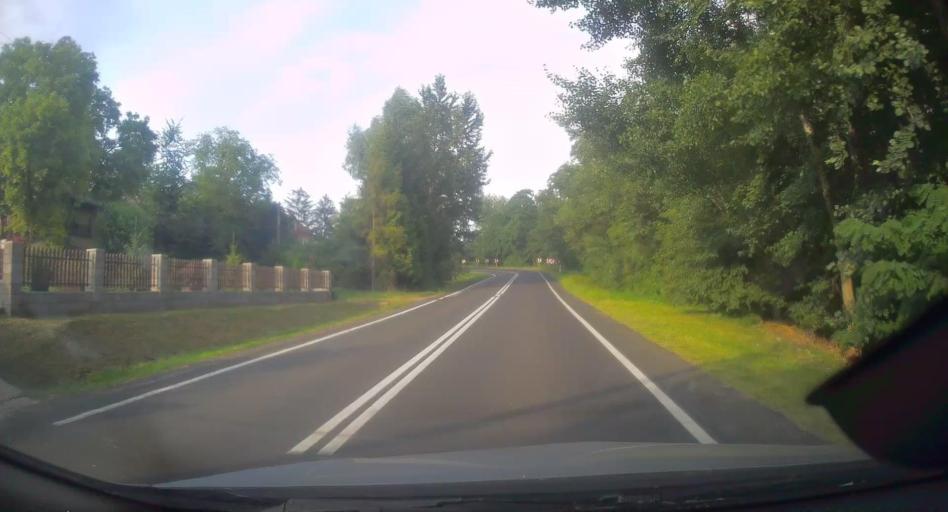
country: PL
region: Lesser Poland Voivodeship
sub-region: Powiat bochenski
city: Dziewin
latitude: 50.1490
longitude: 20.5190
